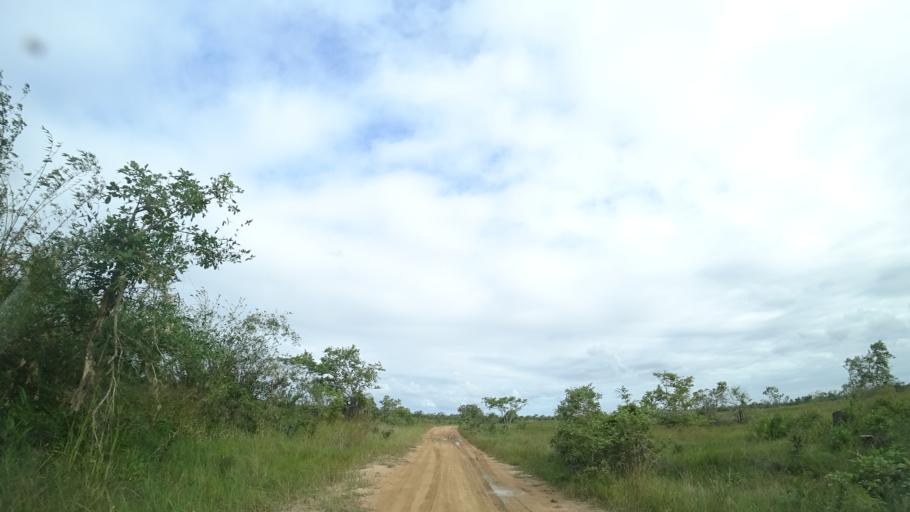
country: MZ
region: Sofala
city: Dondo
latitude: -19.5853
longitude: 35.0867
